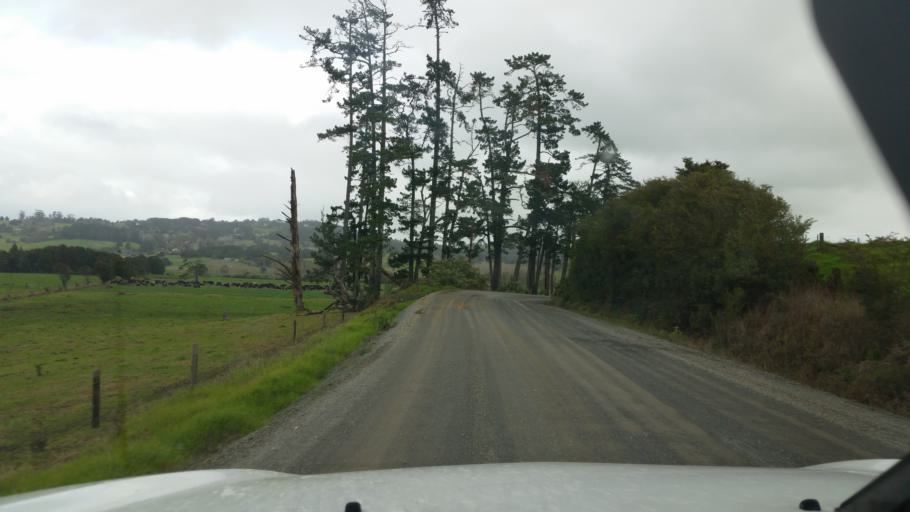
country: NZ
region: Northland
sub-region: Whangarei
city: Maungatapere
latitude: -35.6213
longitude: 174.1979
